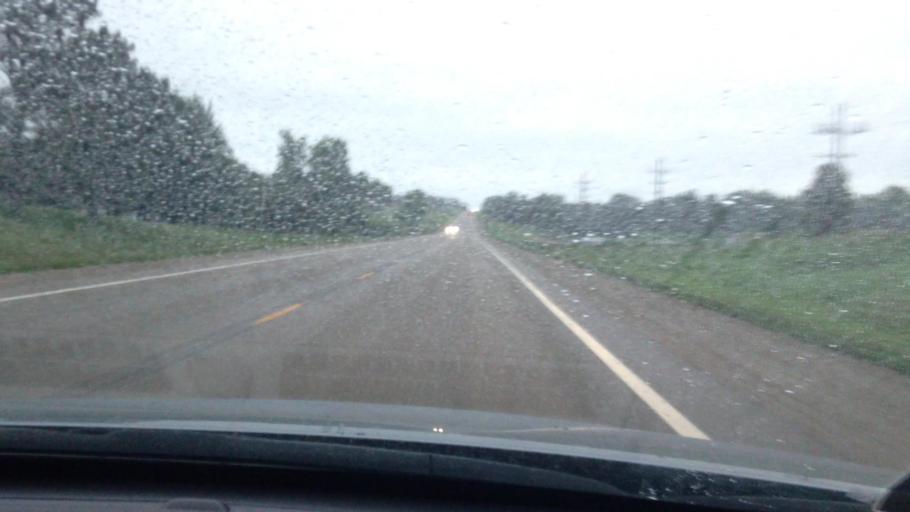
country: US
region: Kansas
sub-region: Brown County
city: Hiawatha
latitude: 39.8287
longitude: -95.5270
